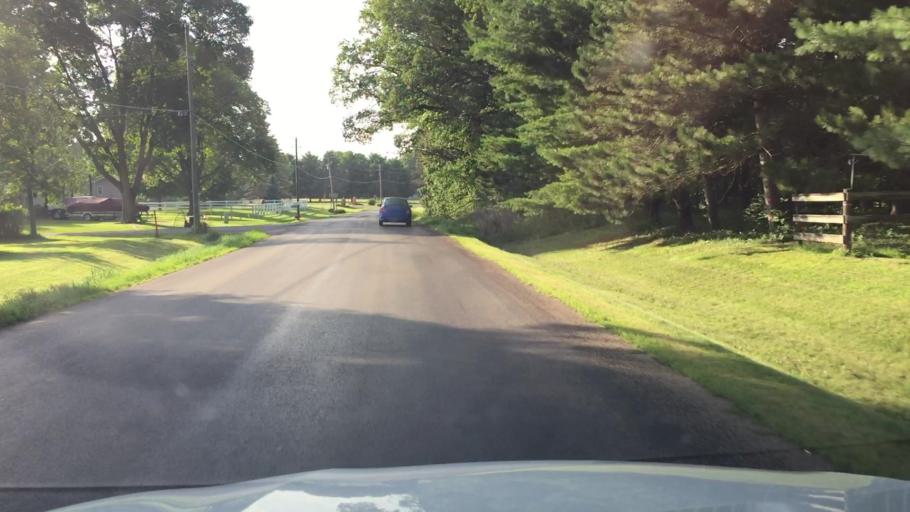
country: US
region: Iowa
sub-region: Linn County
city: Ely
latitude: 41.8213
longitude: -91.6234
